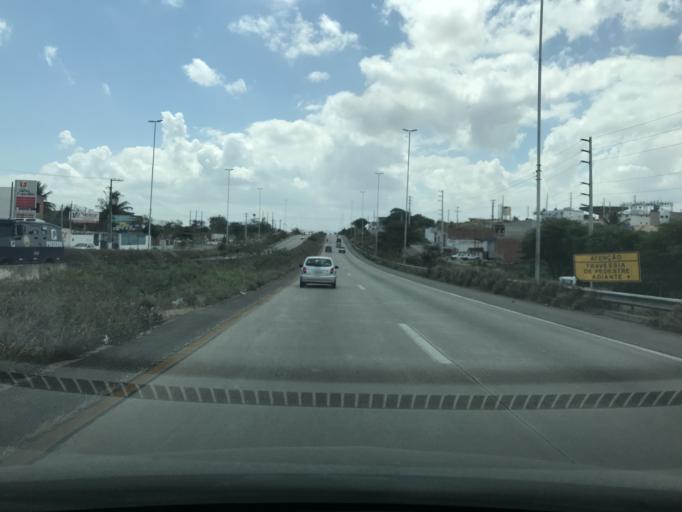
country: BR
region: Pernambuco
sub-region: Caruaru
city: Caruaru
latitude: -8.3033
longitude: -35.9755
